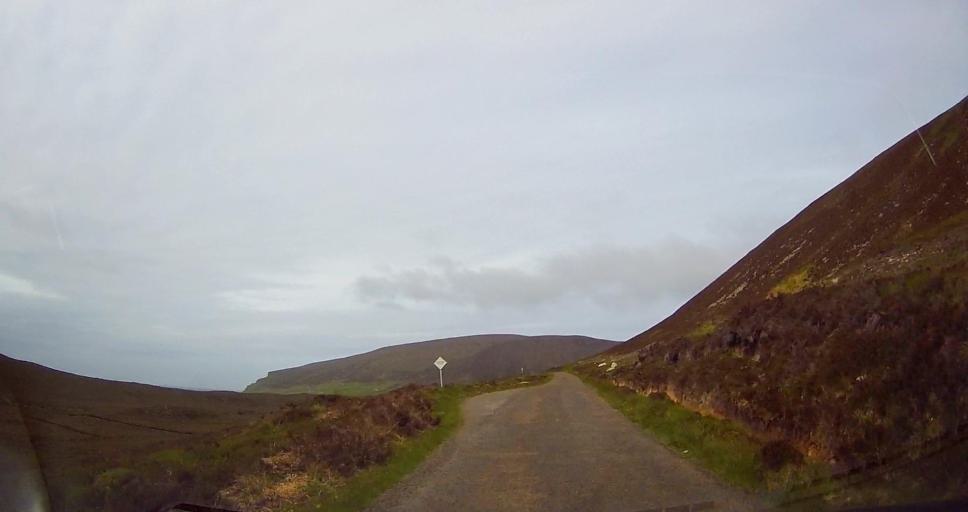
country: GB
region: Scotland
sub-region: Orkney Islands
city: Stromness
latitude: 58.8821
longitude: -3.3571
